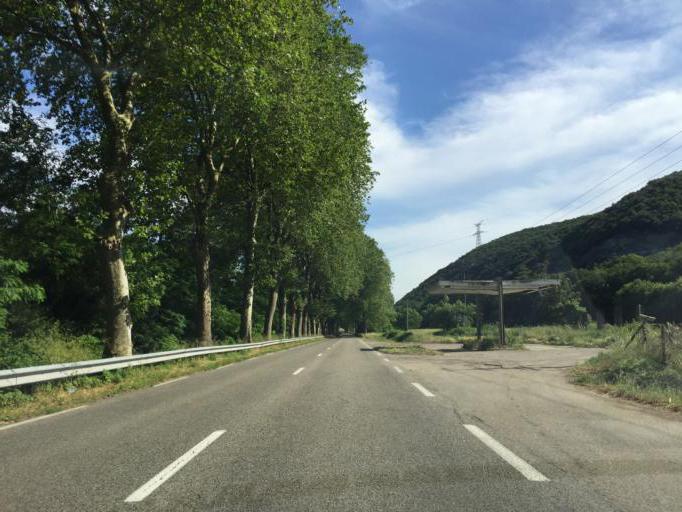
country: FR
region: Rhone-Alpes
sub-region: Departement de la Drome
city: Saulce-sur-Rhone
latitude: 44.6896
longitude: 4.7722
